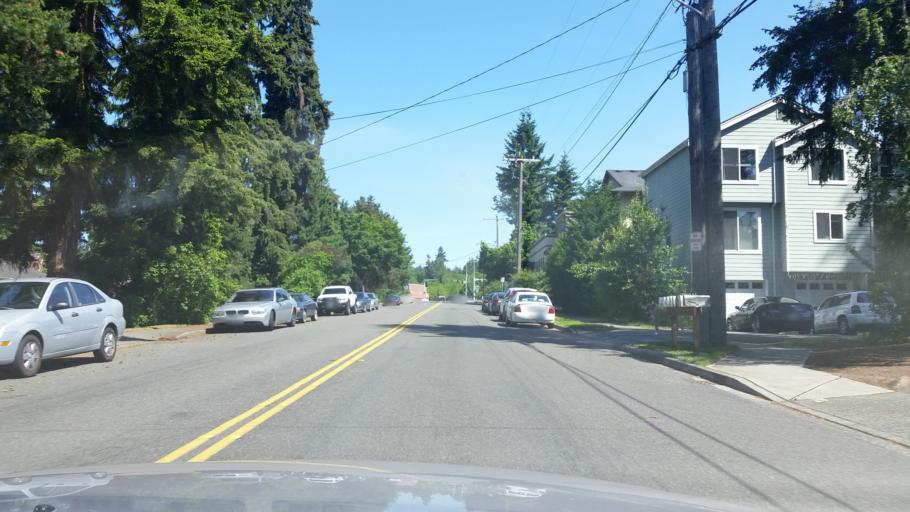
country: US
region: Washington
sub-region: Snohomish County
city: Mountlake Terrace
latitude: 47.7754
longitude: -122.3136
